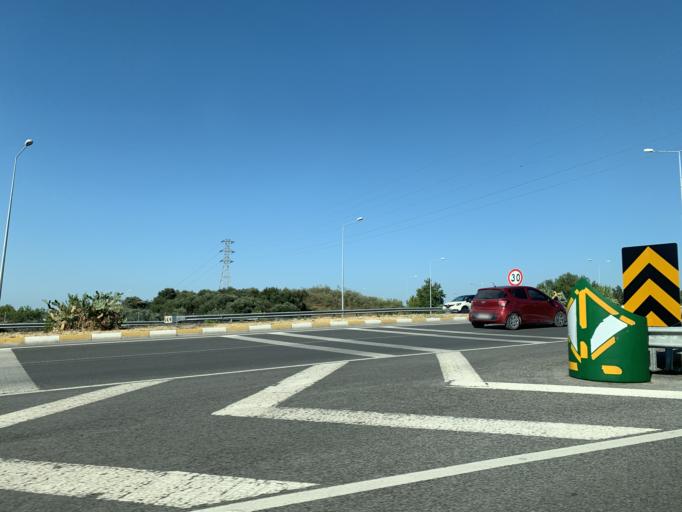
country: TR
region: Izmir
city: Urla
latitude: 38.3254
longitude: 26.7814
